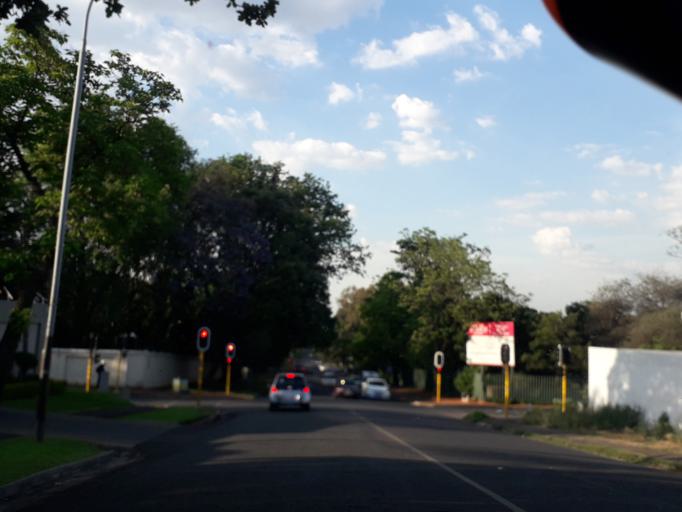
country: ZA
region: Gauteng
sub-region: City of Johannesburg Metropolitan Municipality
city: Johannesburg
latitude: -26.1694
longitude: 28.0650
